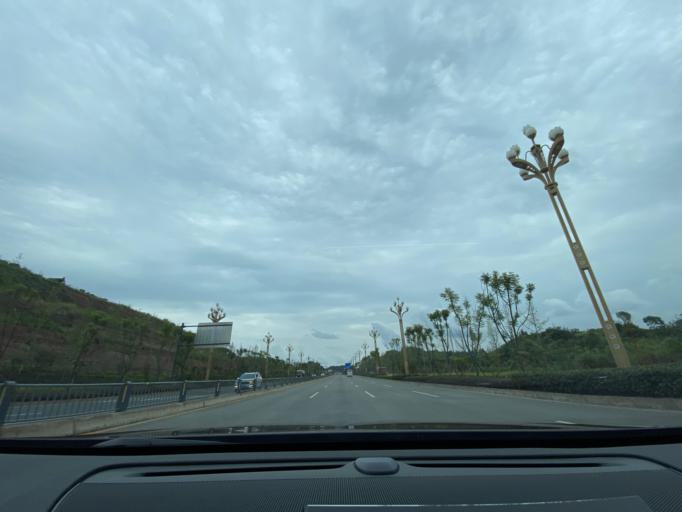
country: CN
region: Sichuan
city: Jiancheng
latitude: 30.4786
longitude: 104.4869
